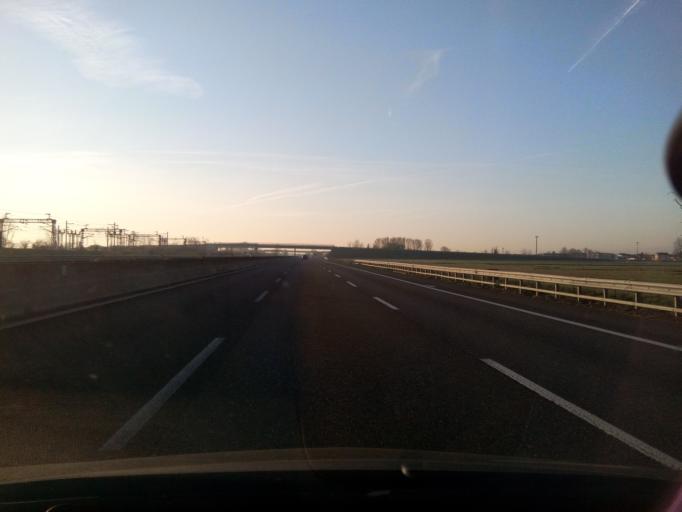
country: IT
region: Lombardy
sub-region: Provincia di Lodi
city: Livraga
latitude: 45.2017
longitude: 9.5477
